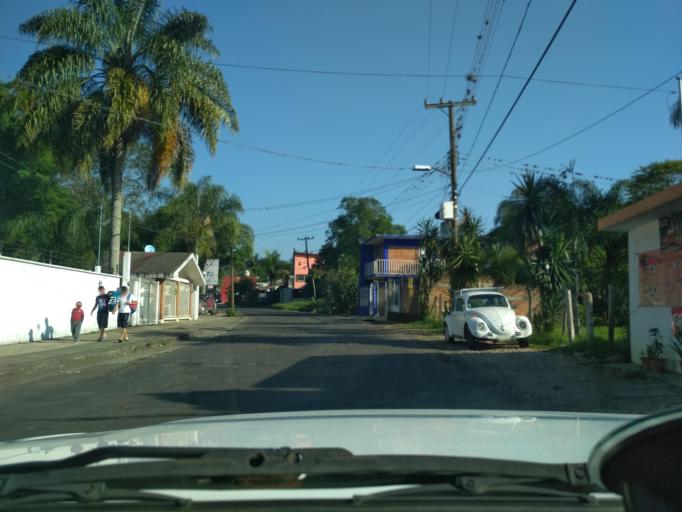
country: MX
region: Veracruz
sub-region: Fortin
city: Fraccionamiento Villas de la Llave
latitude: 18.9191
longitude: -96.9906
